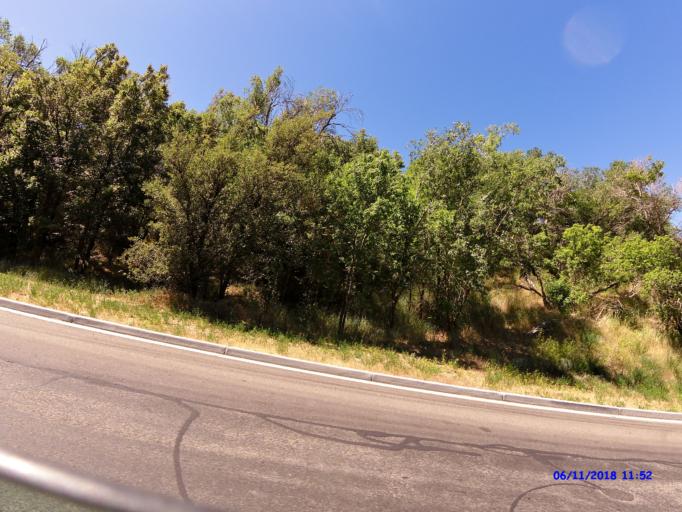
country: US
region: Utah
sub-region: Weber County
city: Ogden
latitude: 41.2351
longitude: -111.9558
